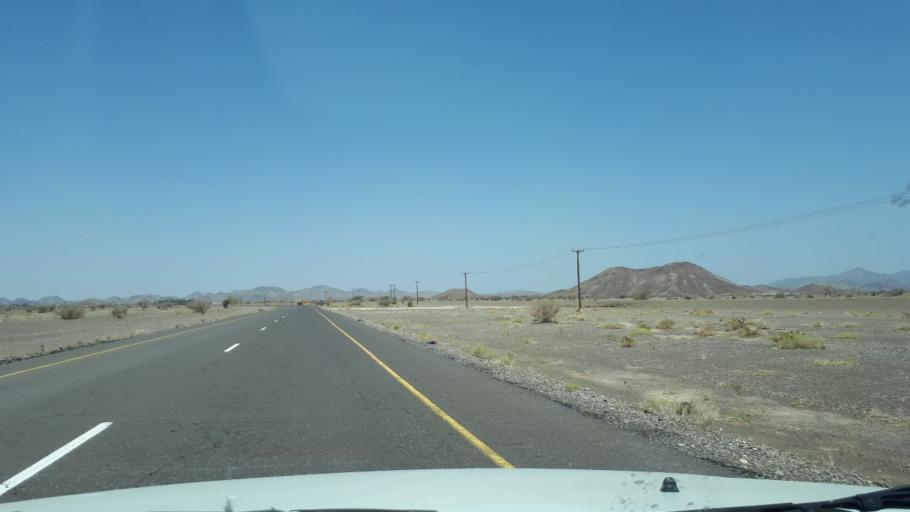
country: OM
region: Ash Sharqiyah
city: Ibra'
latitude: 22.6193
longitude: 58.4152
